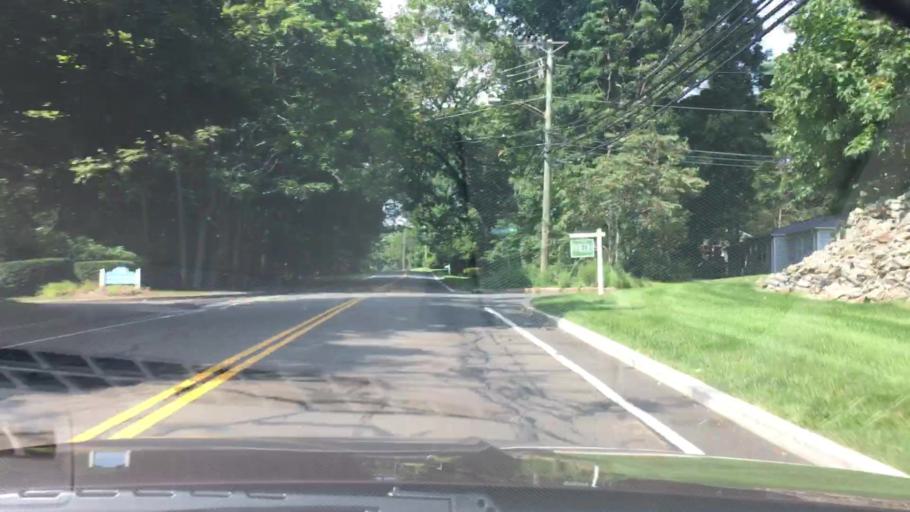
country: US
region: Connecticut
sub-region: Fairfield County
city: Norwalk
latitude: 41.1298
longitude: -73.4130
